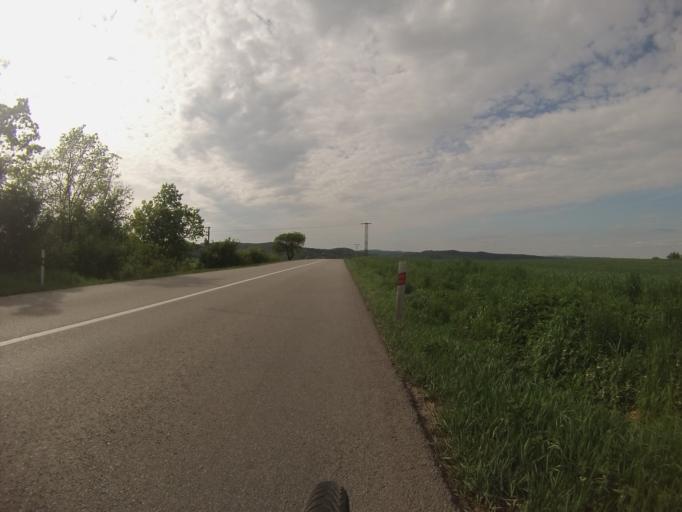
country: CZ
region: South Moravian
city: Veverska Bityska
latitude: 49.2577
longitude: 16.4477
